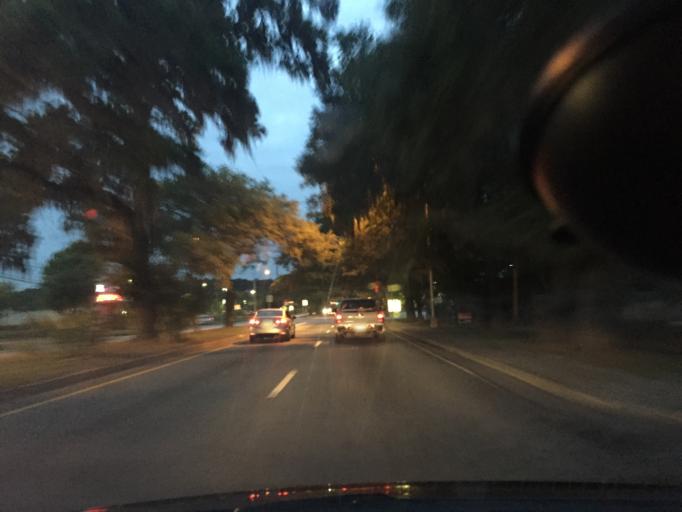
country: US
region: Georgia
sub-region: Chatham County
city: Montgomery
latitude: 31.9995
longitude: -81.1218
